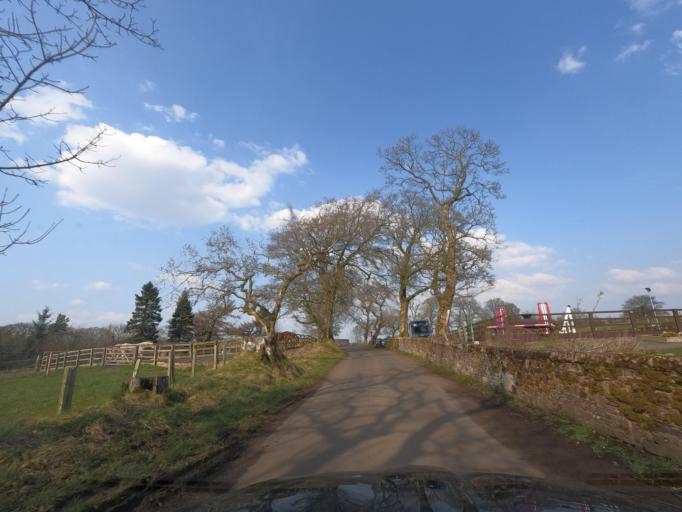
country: GB
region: Scotland
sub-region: South Lanarkshire
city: Carnwath
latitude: 55.7418
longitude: -3.6153
